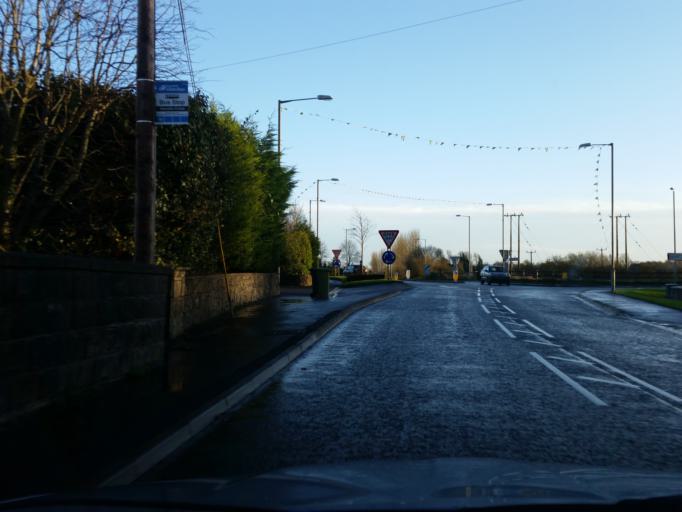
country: IE
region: Ulster
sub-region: An Cabhan
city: Ballyconnell
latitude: 54.1904
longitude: -7.5643
